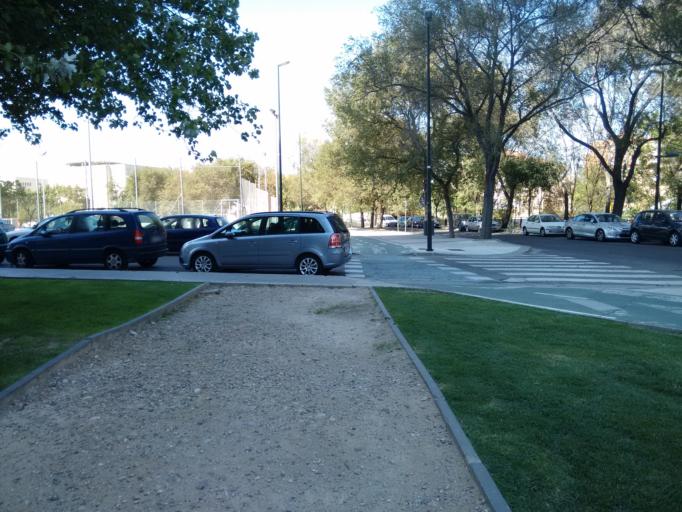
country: ES
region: Aragon
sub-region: Provincia de Zaragoza
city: Zaragoza
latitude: 41.6315
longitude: -0.8817
